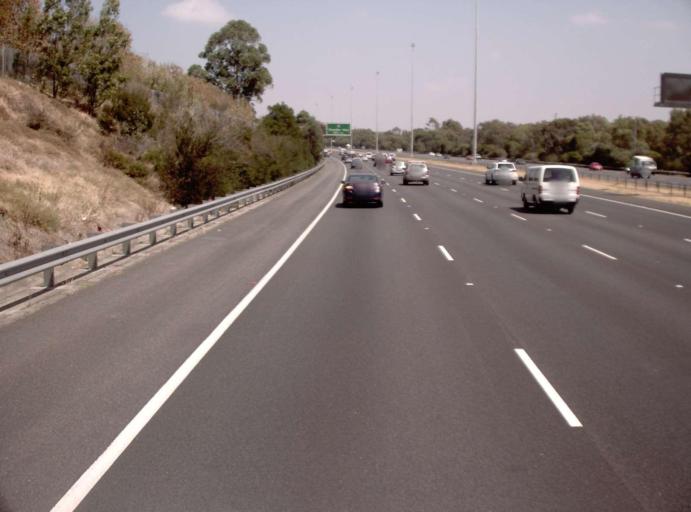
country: AU
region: Victoria
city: Ivanhoe East
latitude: -37.7910
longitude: 145.0457
